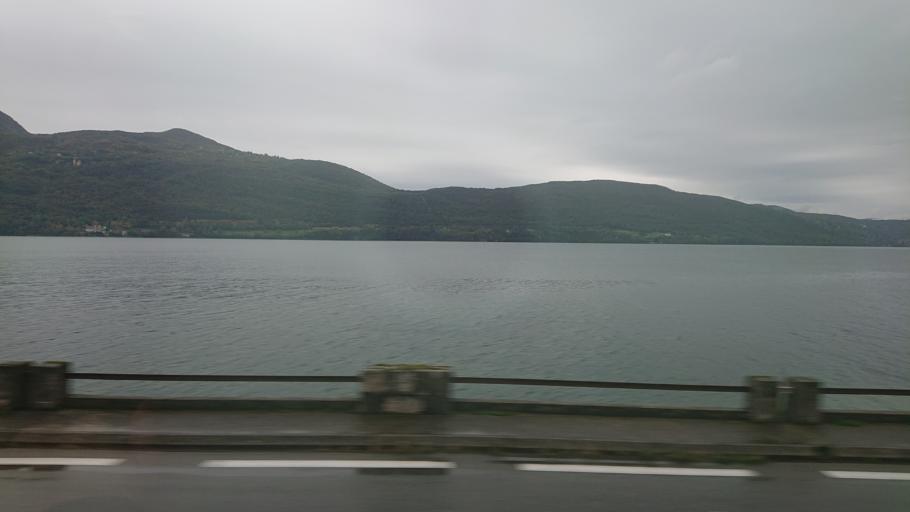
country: FR
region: Rhone-Alpes
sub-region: Departement de la Savoie
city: Chatillon
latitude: 45.7642
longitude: 5.8704
